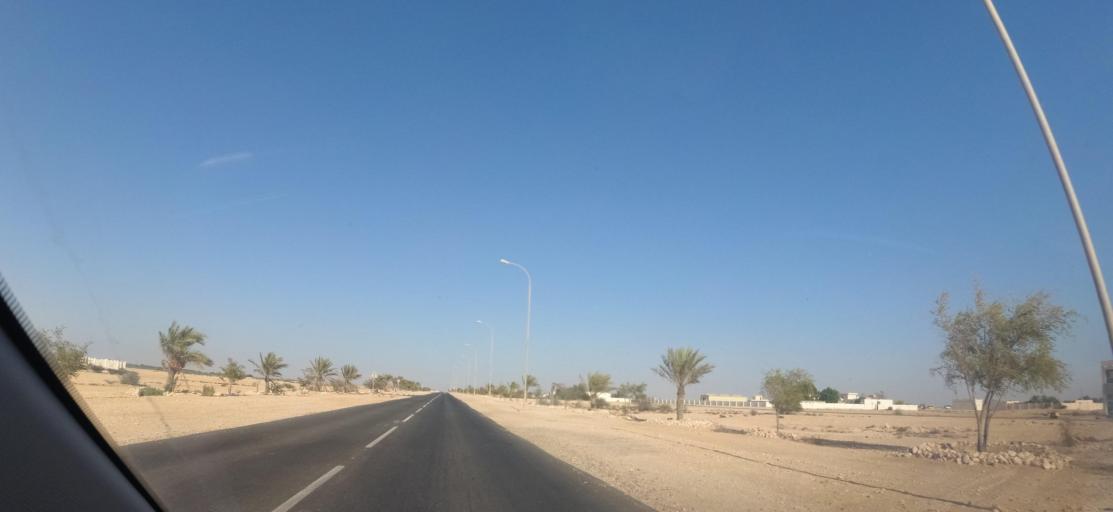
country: QA
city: Al Ghuwayriyah
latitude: 25.8307
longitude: 51.2505
